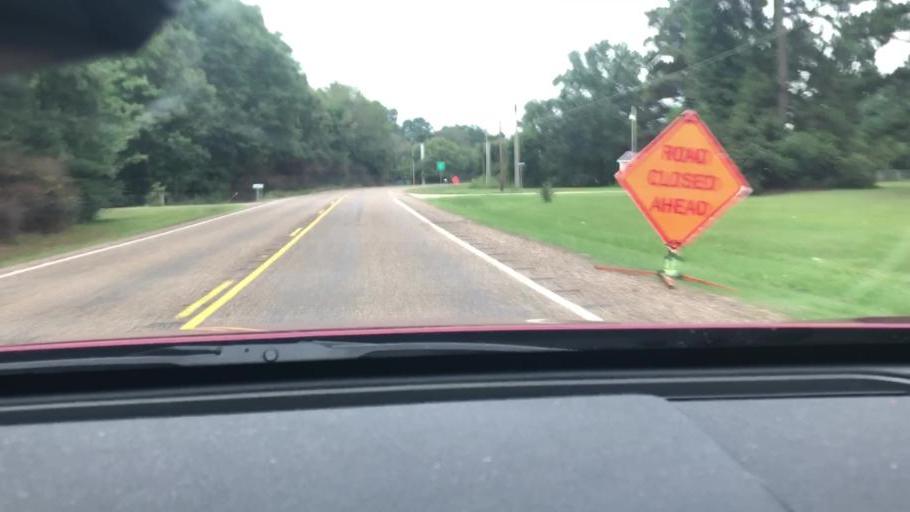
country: US
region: Texas
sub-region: Bowie County
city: Wake Village
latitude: 33.3828
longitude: -94.1060
